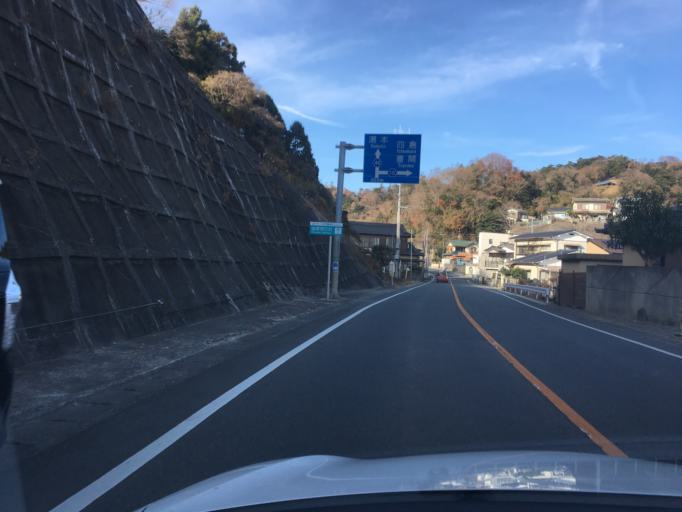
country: JP
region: Fukushima
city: Iwaki
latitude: 36.9738
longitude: 140.9544
